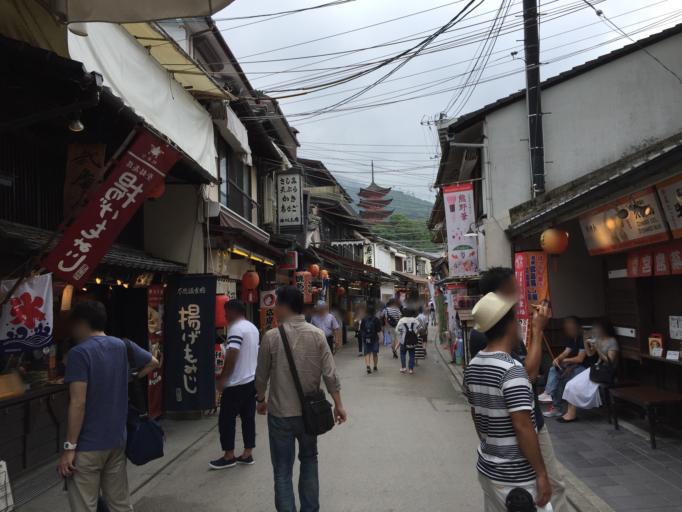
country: JP
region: Hiroshima
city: Miyajima
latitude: 34.2986
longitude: 132.3216
